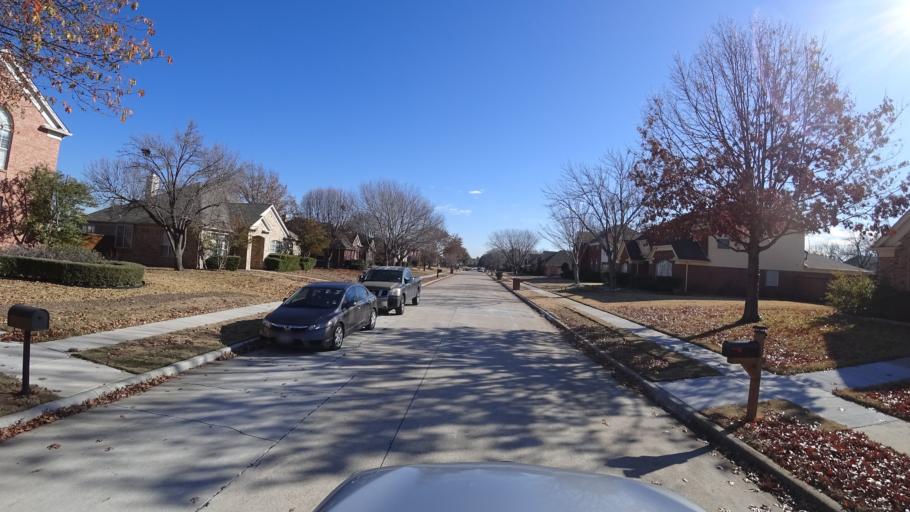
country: US
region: Texas
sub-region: Denton County
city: Lewisville
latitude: 33.0202
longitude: -97.0345
